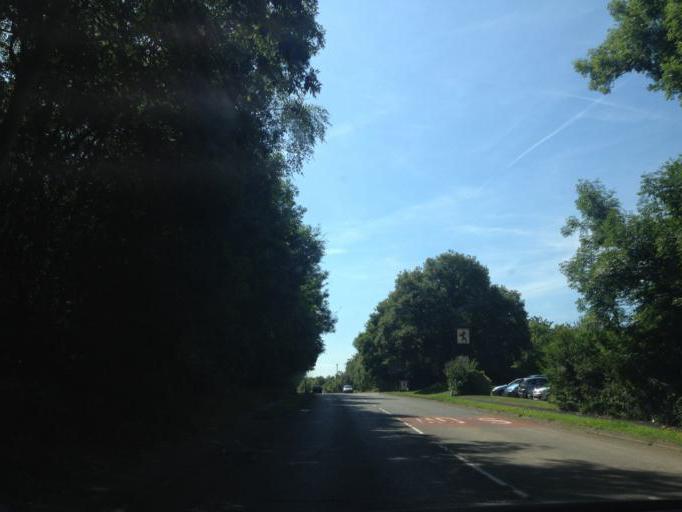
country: GB
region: England
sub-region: Hertfordshire
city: Welwyn Garden City
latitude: 51.8132
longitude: -0.2249
